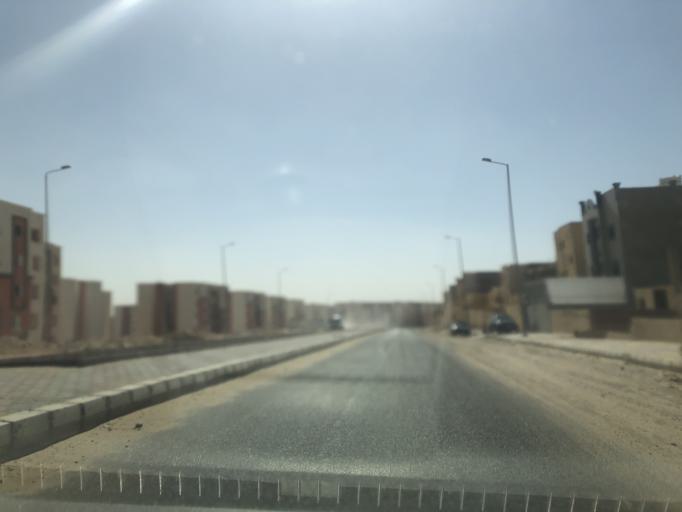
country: EG
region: Al Jizah
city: Madinat Sittah Uktubar
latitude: 29.9270
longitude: 30.9993
